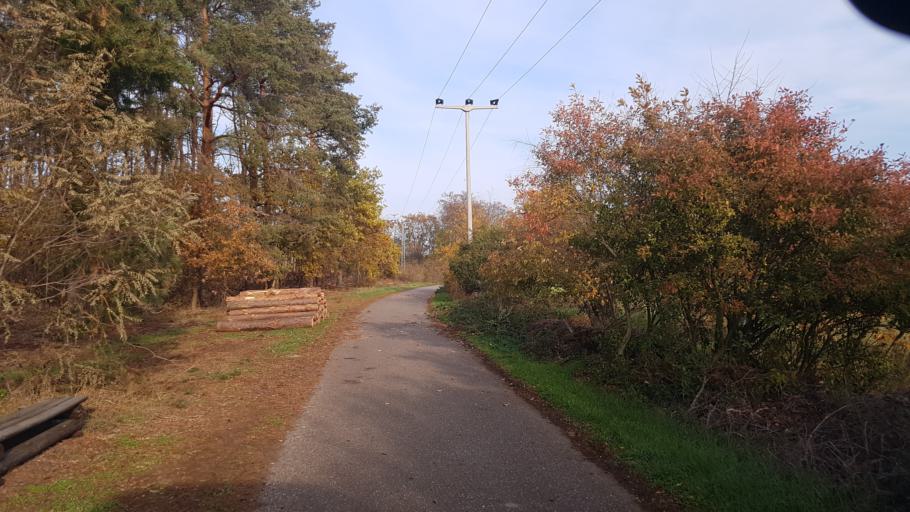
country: DE
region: Brandenburg
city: Falkenberg
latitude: 51.5995
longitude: 13.2796
